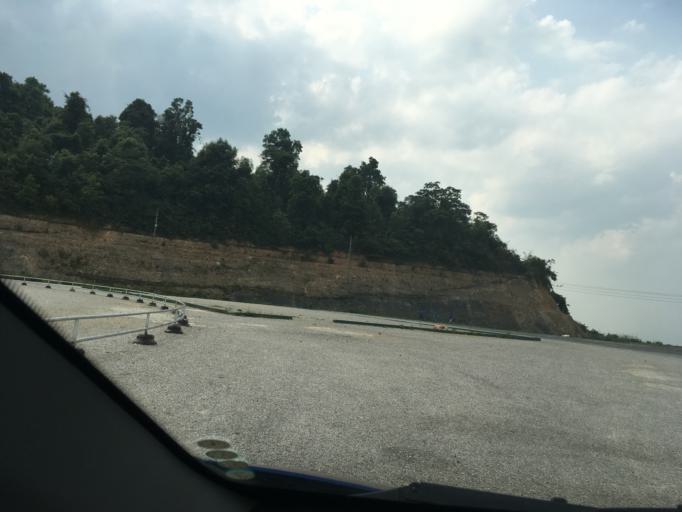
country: LA
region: Phongsali
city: Phongsali
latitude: 21.6832
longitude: 102.0996
